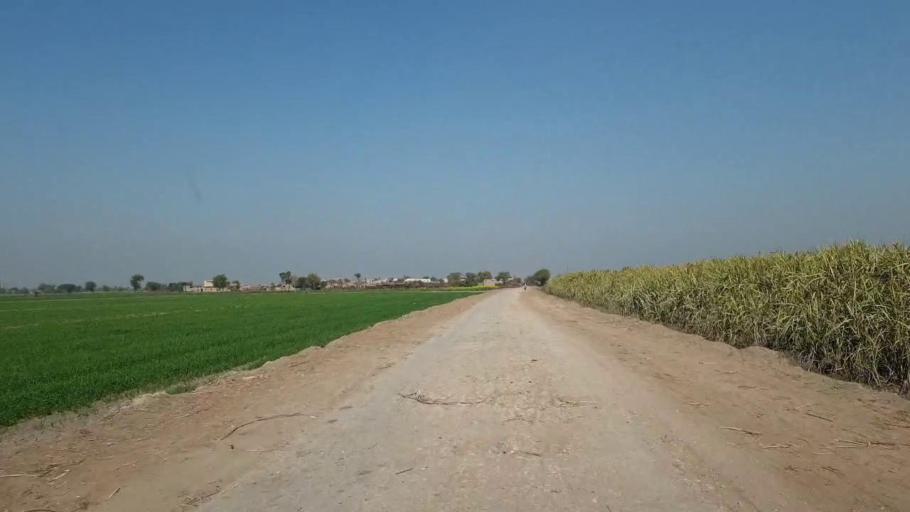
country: PK
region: Sindh
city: Shahdadpur
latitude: 25.9488
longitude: 68.5111
